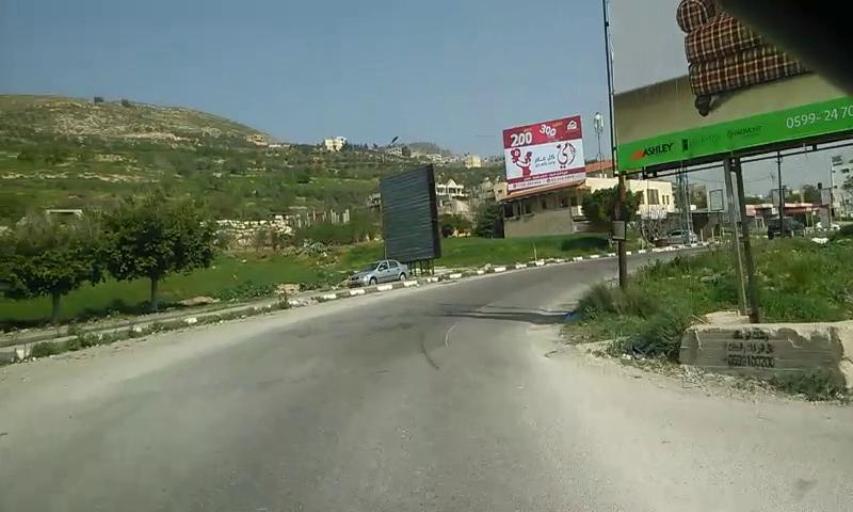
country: PS
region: West Bank
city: Kafr Qallil
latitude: 32.1827
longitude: 35.2771
